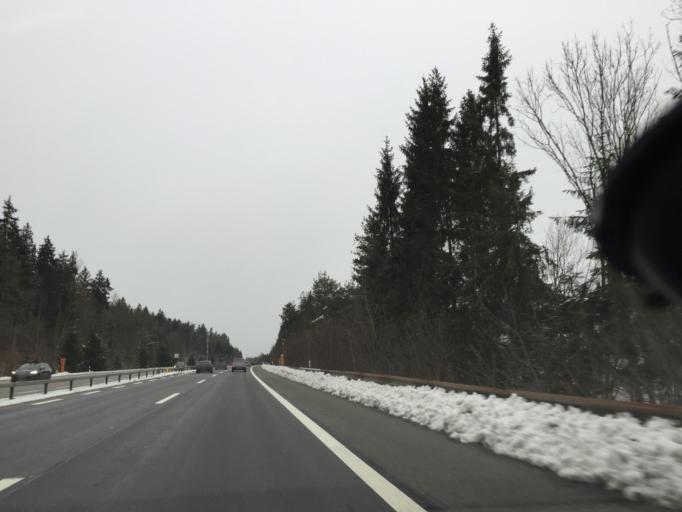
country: CH
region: Zurich
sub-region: Bezirk Horgen
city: Oberrieden / Mitte
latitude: 47.2654
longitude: 8.5747
